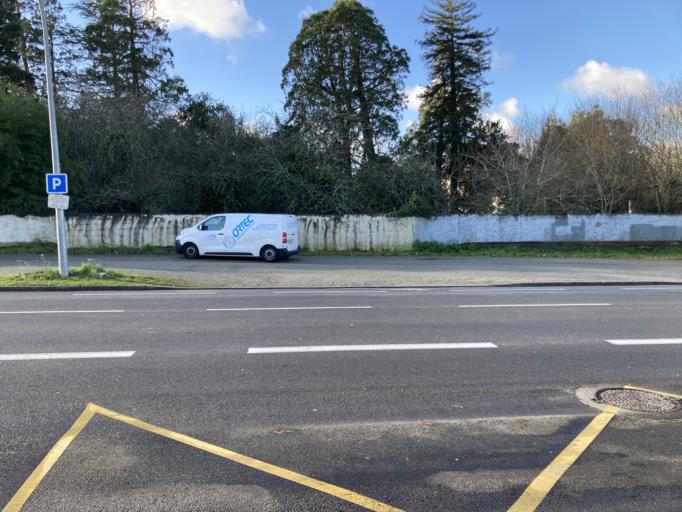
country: FR
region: Pays de la Loire
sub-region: Departement de la Loire-Atlantique
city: Saint-Sebastien-sur-Loire
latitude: 47.2106
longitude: -1.4903
